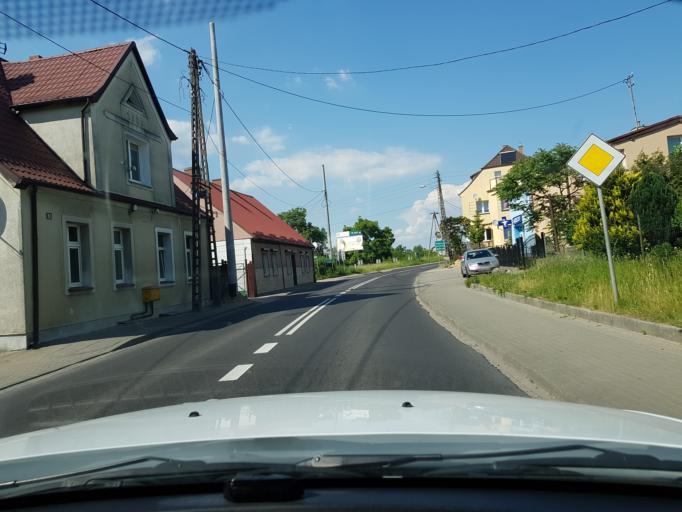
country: PL
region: West Pomeranian Voivodeship
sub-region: Powiat gryfinski
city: Gryfino
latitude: 53.3179
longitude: 14.5359
